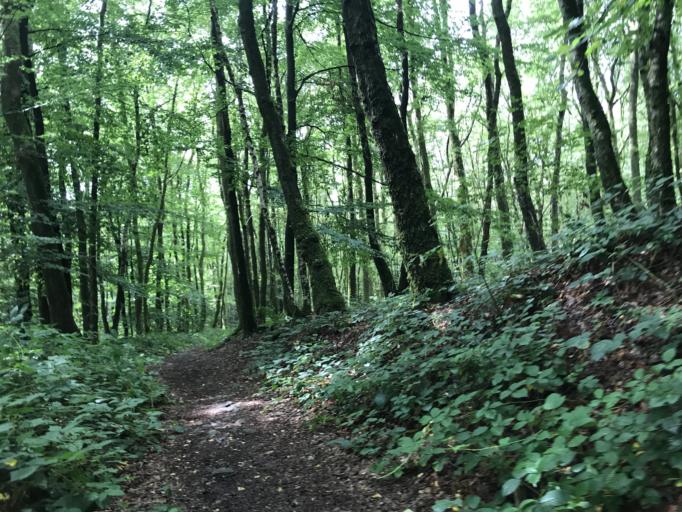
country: FR
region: Champagne-Ardenne
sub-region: Departement des Ardennes
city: Thilay
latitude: 49.8894
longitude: 4.7851
